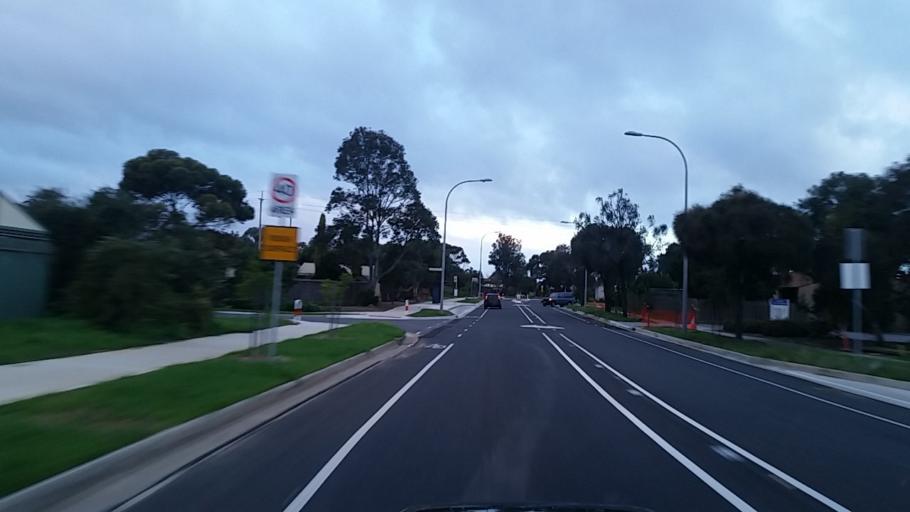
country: AU
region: South Australia
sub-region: Charles Sturt
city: West Lakes Shore
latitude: -34.8562
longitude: 138.4944
